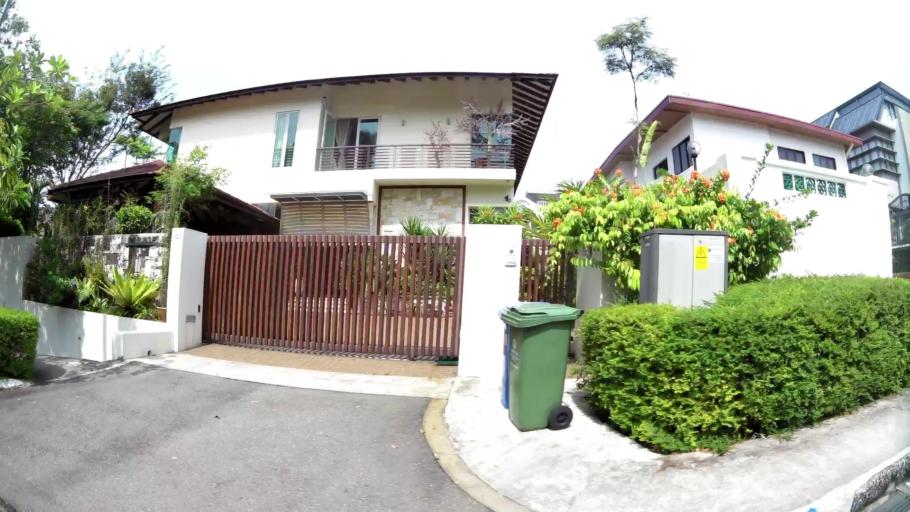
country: SG
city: Singapore
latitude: 1.3268
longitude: 103.7659
